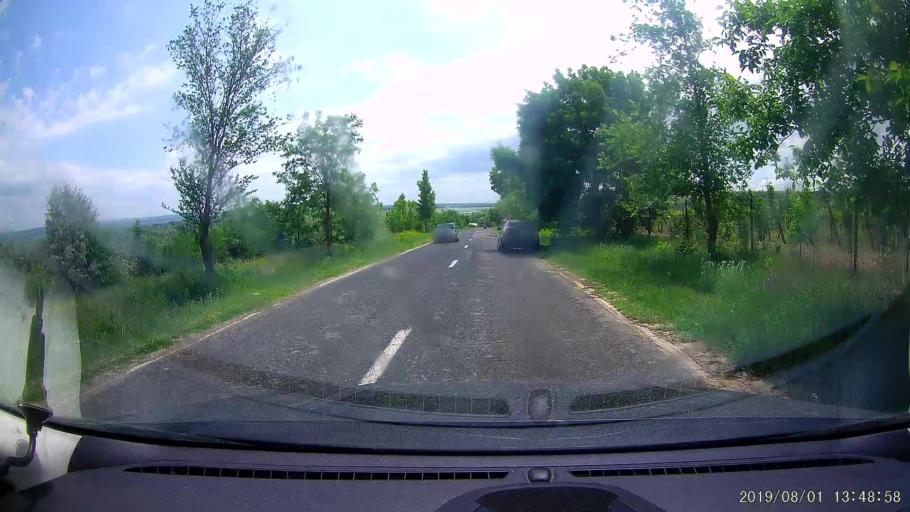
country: RO
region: Galati
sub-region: Comuna Oancea
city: Oancea
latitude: 45.9002
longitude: 28.1092
